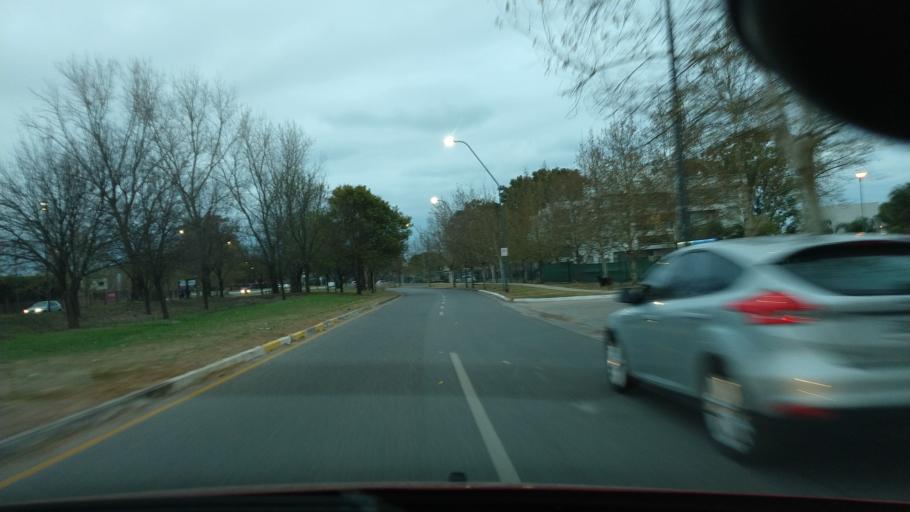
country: AR
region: Cordoba
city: La Calera
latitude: -31.3712
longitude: -64.2771
